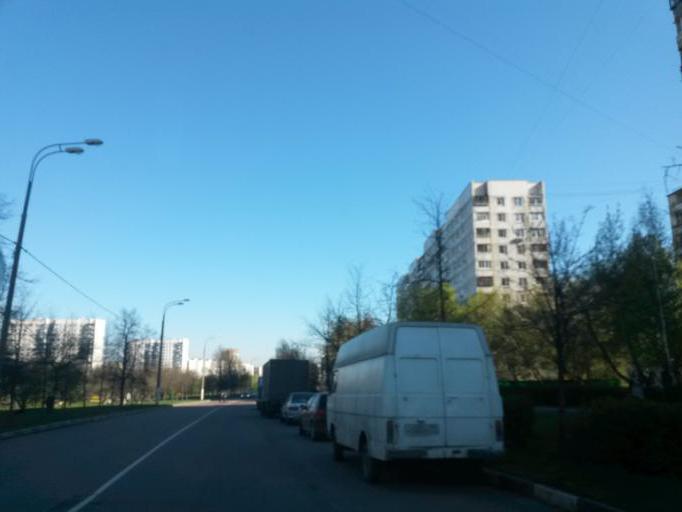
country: RU
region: Moscow
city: Orekhovo-Borisovo
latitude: 55.6163
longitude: 37.7301
